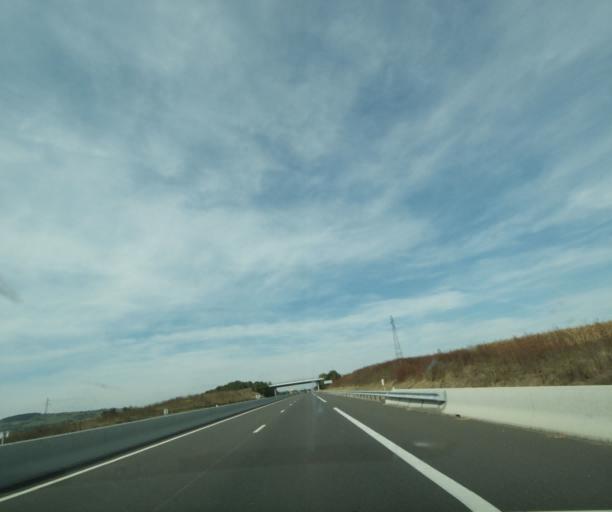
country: FR
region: Auvergne
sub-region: Departement de l'Allier
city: Gannat
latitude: 46.1062
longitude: 3.2253
